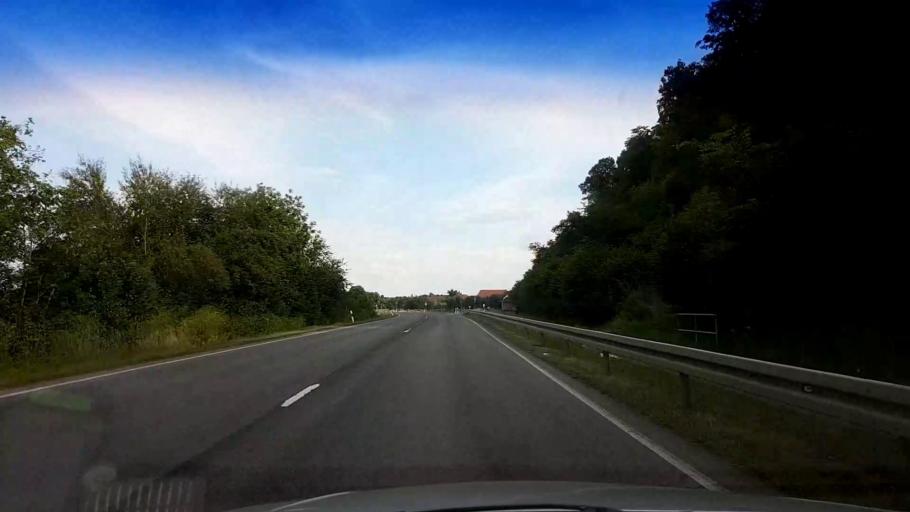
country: DE
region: Bavaria
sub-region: Regierungsbezirk Unterfranken
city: Stettfeld
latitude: 49.9613
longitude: 10.7104
